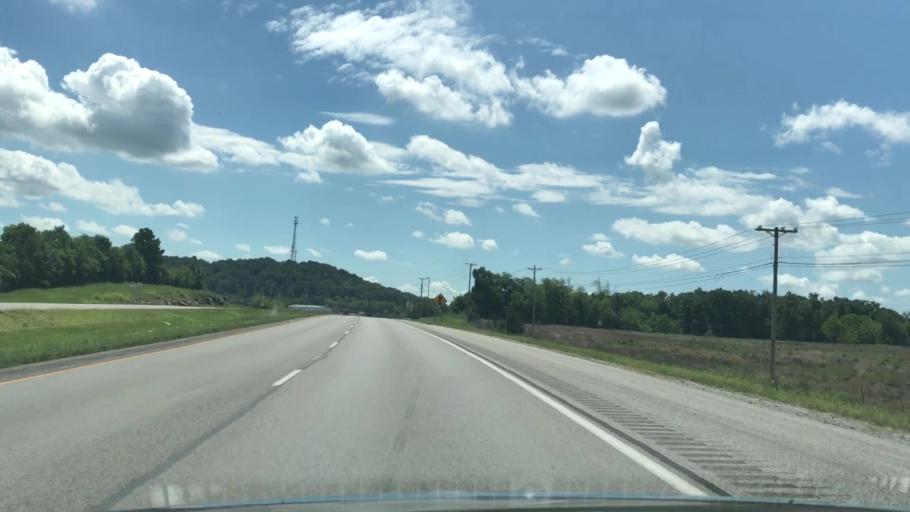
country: US
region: Kentucky
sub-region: Logan County
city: Russellville
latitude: 36.8423
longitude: -86.9198
